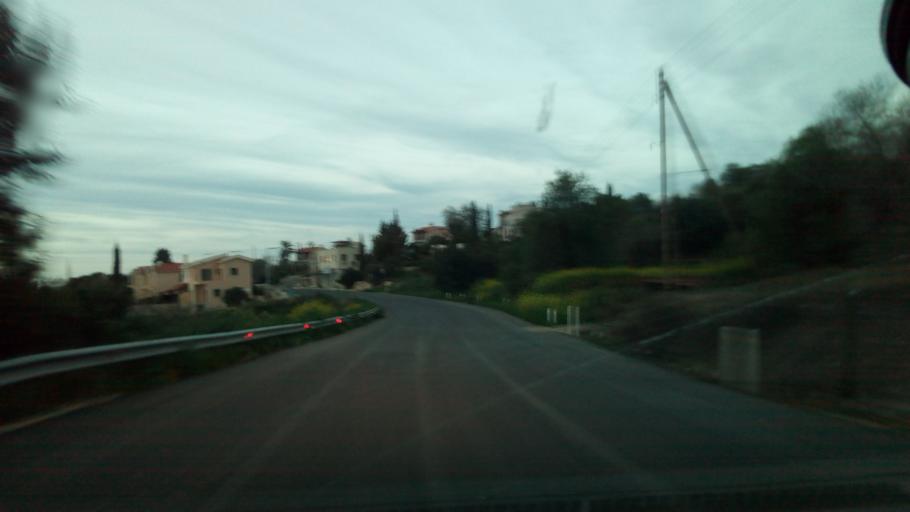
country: CY
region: Pafos
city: Polis
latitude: 34.9894
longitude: 32.5065
